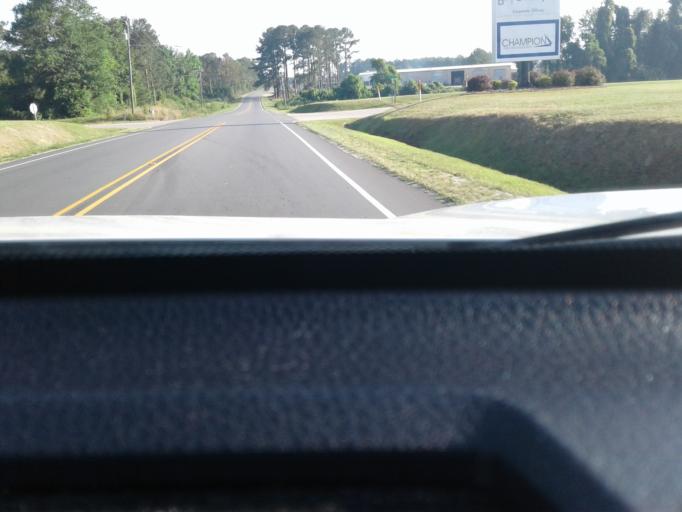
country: US
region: North Carolina
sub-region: Harnett County
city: Dunn
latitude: 35.3202
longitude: -78.6307
